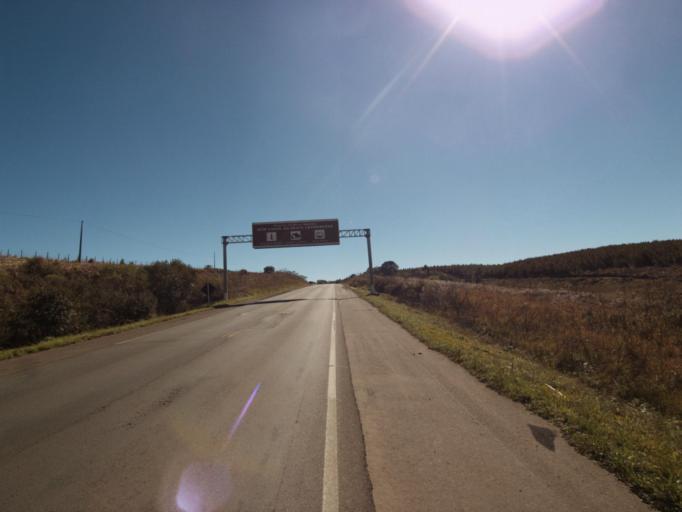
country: BR
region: Santa Catarina
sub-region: Concordia
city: Concordia
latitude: -26.9281
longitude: -51.8755
